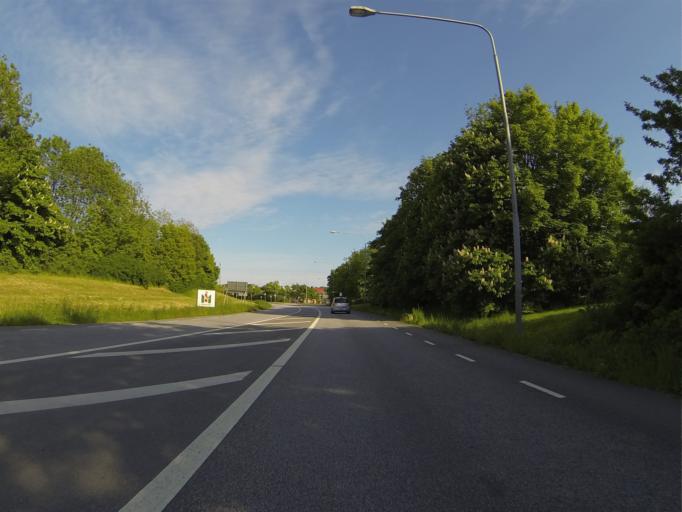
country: SE
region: Skane
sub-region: Burlovs Kommun
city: Arloev
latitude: 55.6094
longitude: 13.0716
